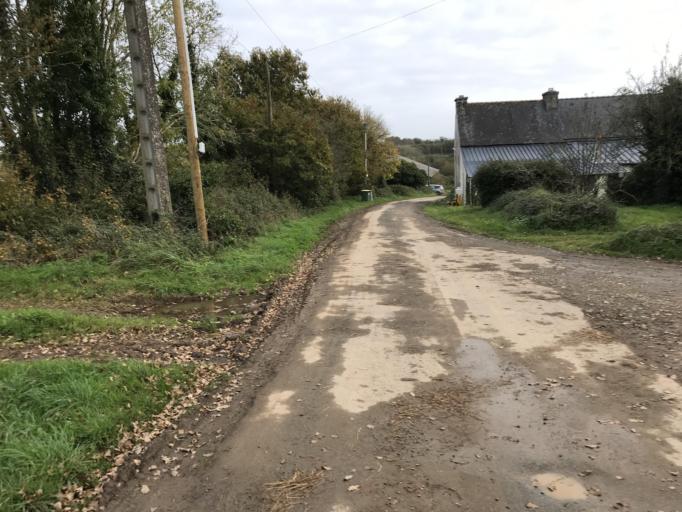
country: FR
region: Brittany
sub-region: Departement du Finistere
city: Hopital-Camfrout
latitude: 48.3294
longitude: -4.2067
